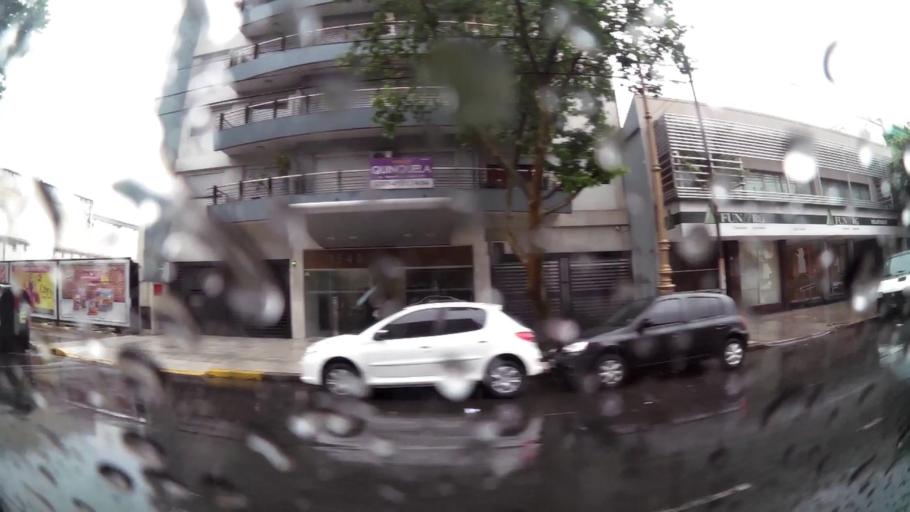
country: AR
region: Buenos Aires
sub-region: Partido de Avellaneda
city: Avellaneda
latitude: -34.6452
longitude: -58.3733
